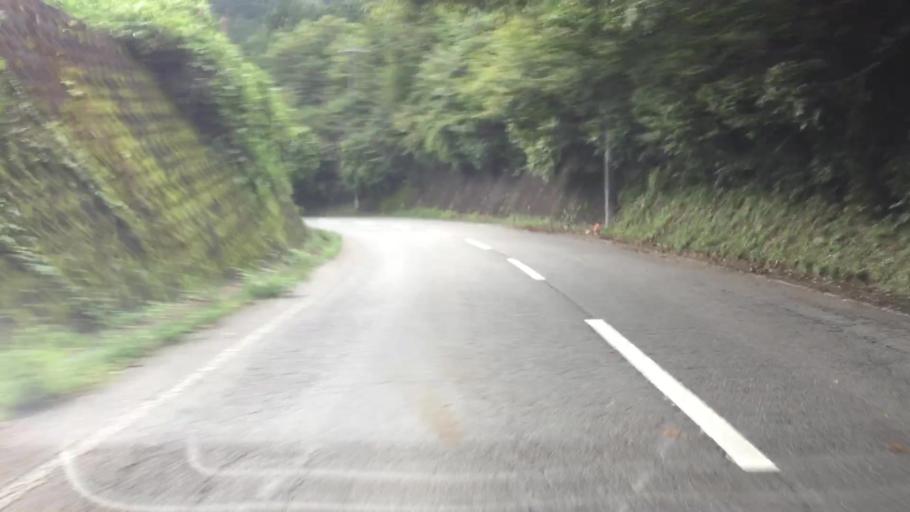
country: JP
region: Tochigi
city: Imaichi
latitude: 36.7570
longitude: 139.6622
